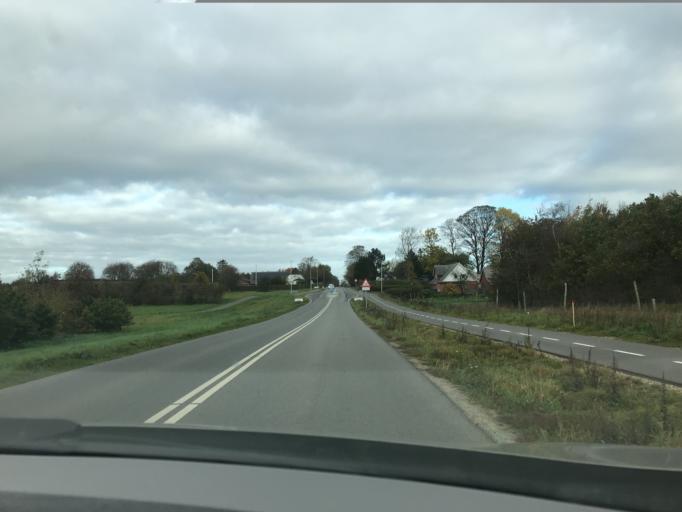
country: DK
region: South Denmark
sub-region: Kolding Kommune
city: Kolding
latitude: 55.5538
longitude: 9.4108
